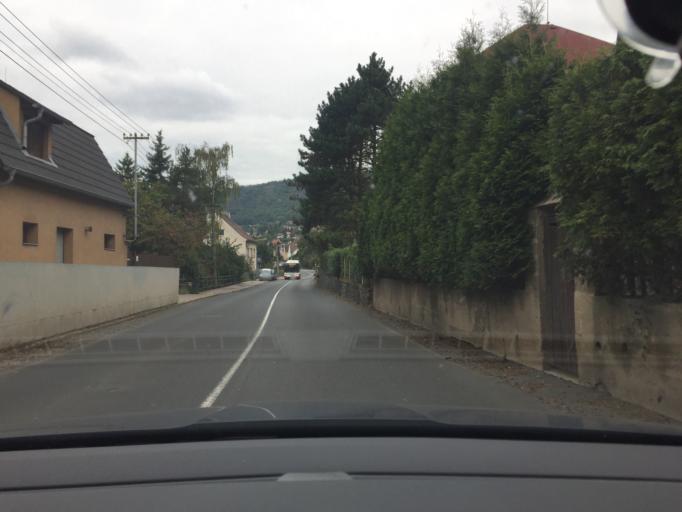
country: CZ
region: Ustecky
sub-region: Okres Usti nad Labem
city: Usti nad Labem
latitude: 50.6208
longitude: 14.0784
